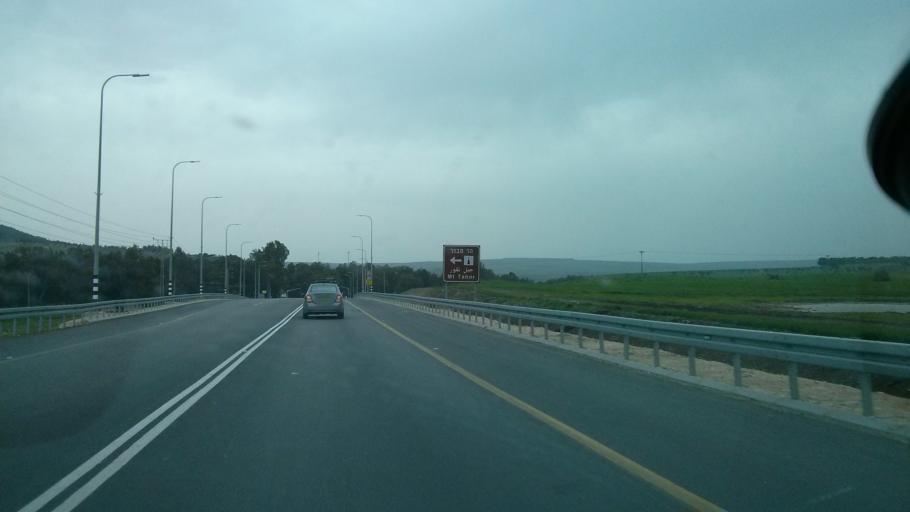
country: IL
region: Northern District
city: Shibli
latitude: 32.6606
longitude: 35.3901
